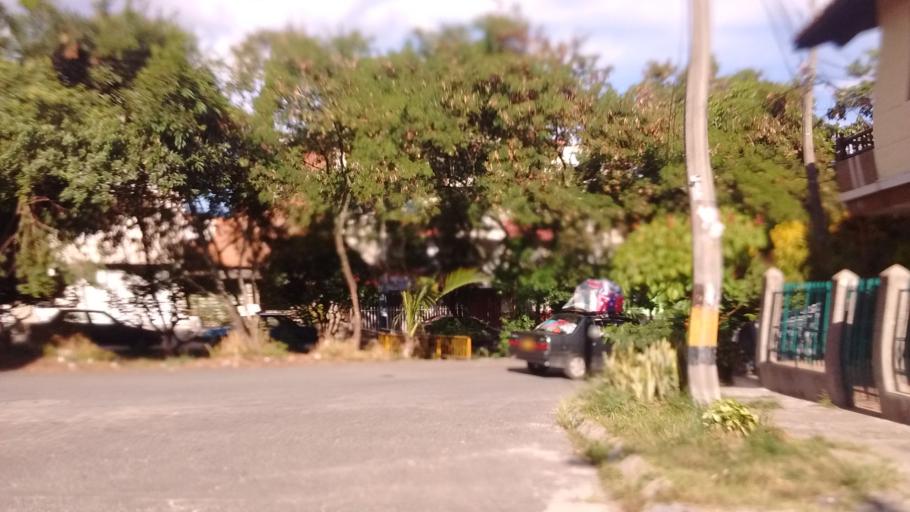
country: CO
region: Antioquia
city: Medellin
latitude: 6.2599
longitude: -75.6122
